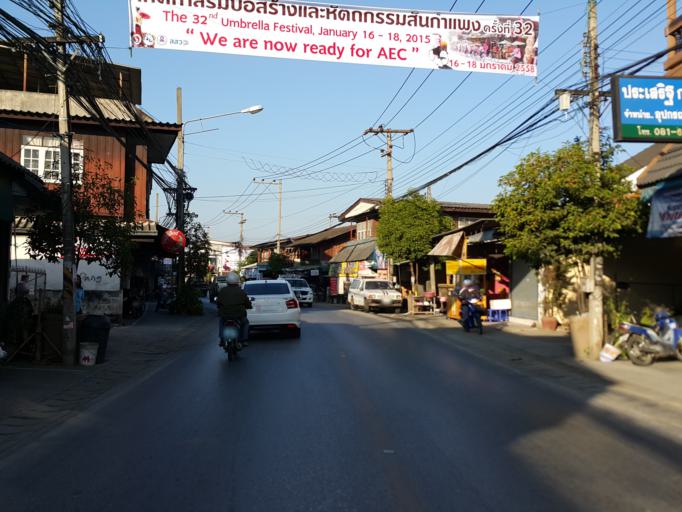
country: TH
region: Chiang Mai
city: San Kamphaeng
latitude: 18.7670
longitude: 99.0836
